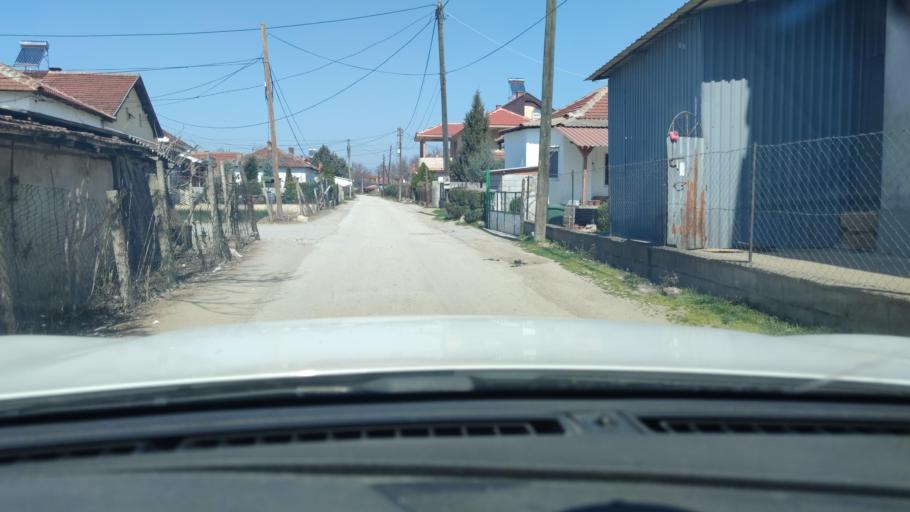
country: MK
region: Rosoman
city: Rosoman
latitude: 41.5188
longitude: 21.9408
